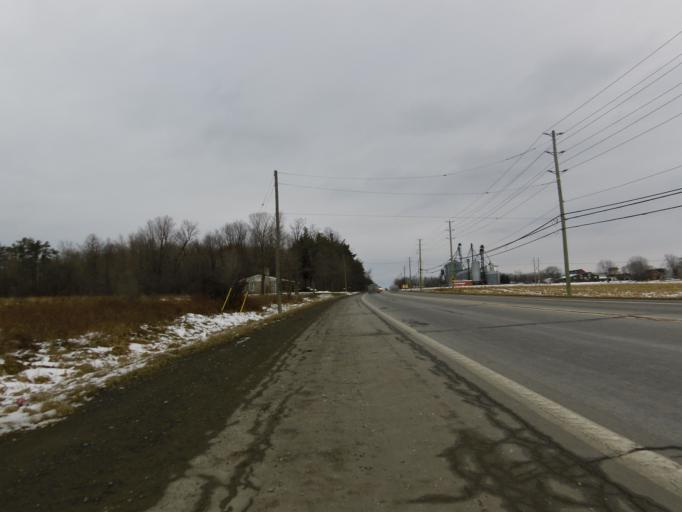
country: CA
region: Ontario
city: Bells Corners
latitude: 45.2646
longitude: -75.8158
